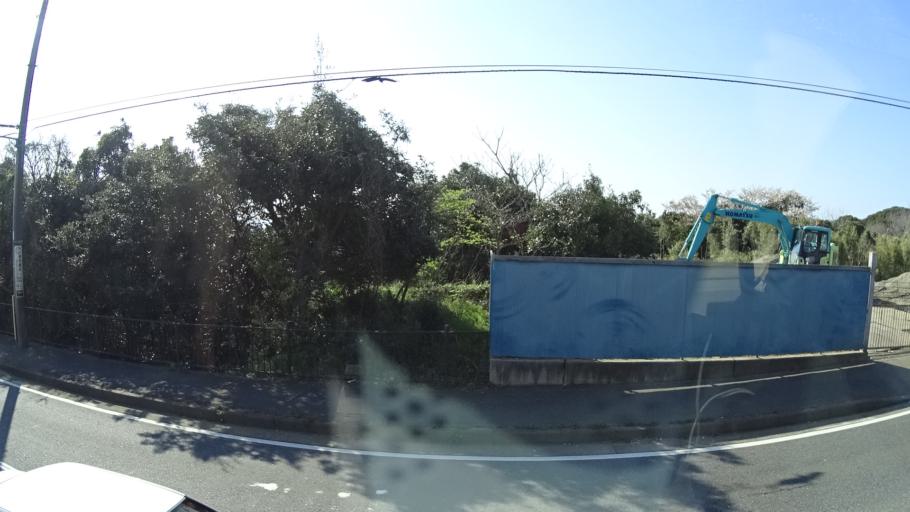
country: JP
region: Kanagawa
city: Miura
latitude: 35.1649
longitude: 139.6429
